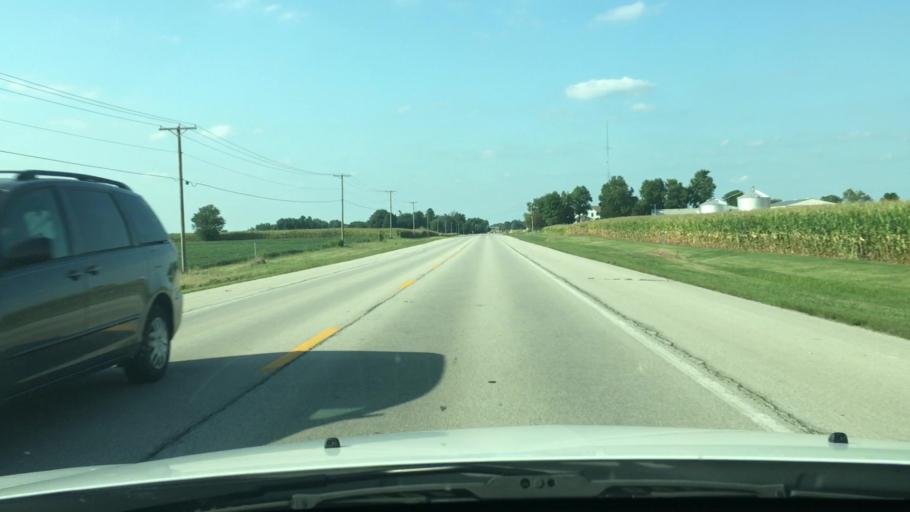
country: US
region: Illinois
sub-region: DeKalb County
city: DeKalb
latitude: 41.8837
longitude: -88.7538
